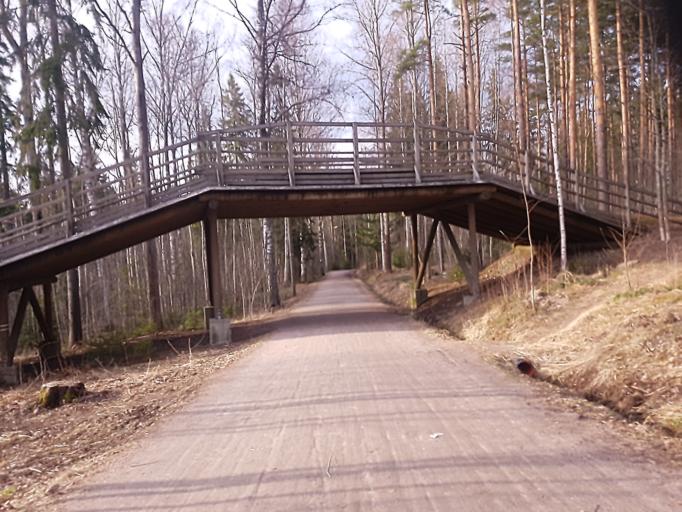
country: FI
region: Uusimaa
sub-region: Helsinki
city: Helsinki
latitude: 60.2577
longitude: 24.9125
